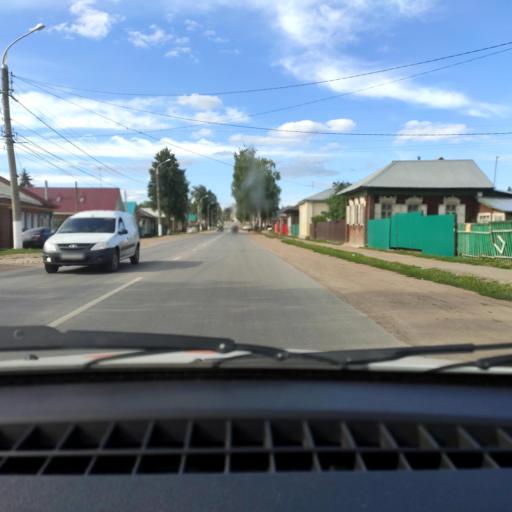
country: RU
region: Bashkortostan
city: Blagoveshchensk
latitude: 55.0367
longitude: 55.9641
